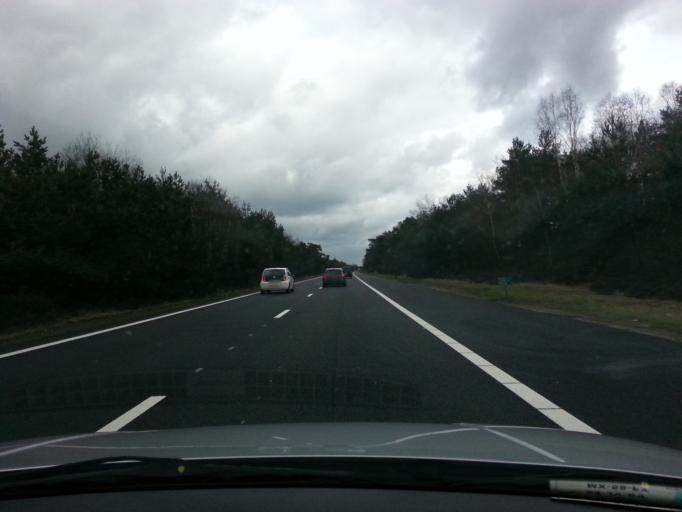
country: NL
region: Gelderland
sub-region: Gemeente Oldebroek
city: Oldebroek
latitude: 52.4241
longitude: 5.9225
